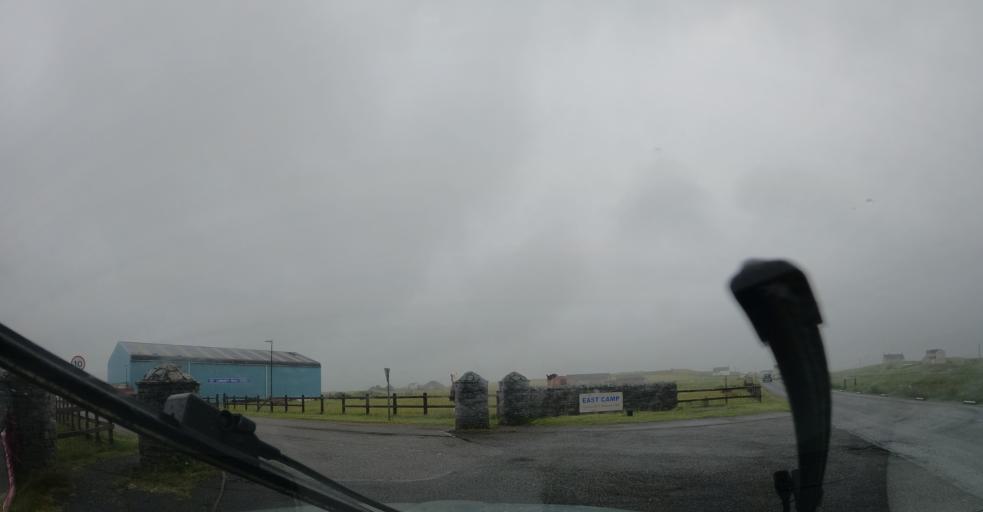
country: GB
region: Scotland
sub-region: Eilean Siar
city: Benbecula
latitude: 57.4718
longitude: -7.3650
